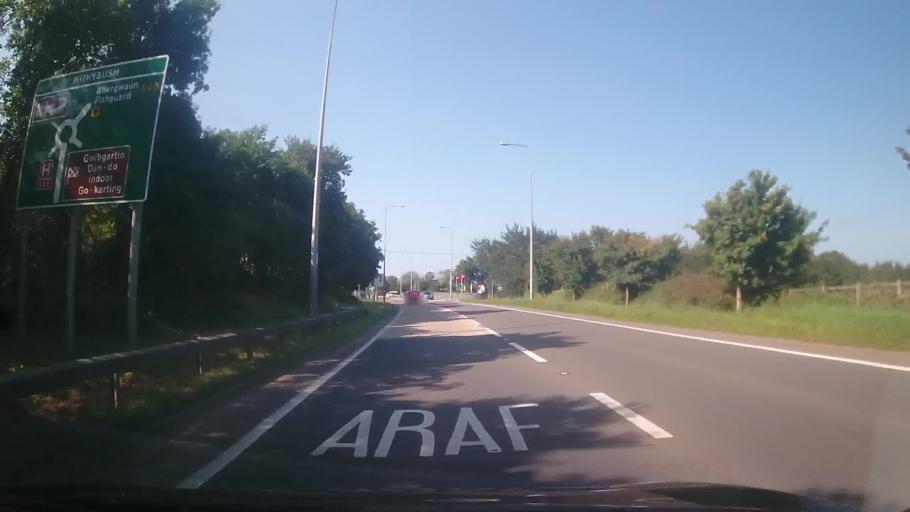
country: GB
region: Wales
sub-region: Pembrokeshire
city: Haverfordwest
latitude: 51.8176
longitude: -4.9598
